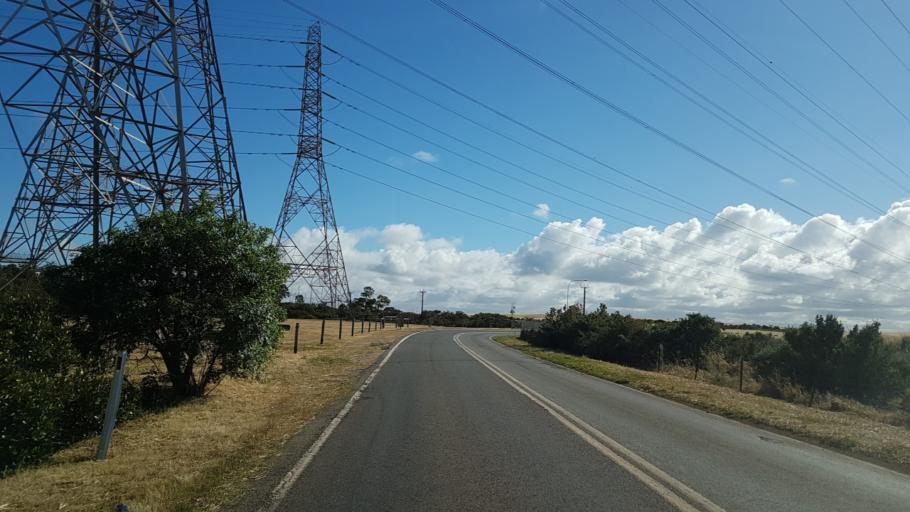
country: AU
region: South Australia
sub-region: Port Adelaide Enfield
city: Birkenhead
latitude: -34.8085
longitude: 138.5284
